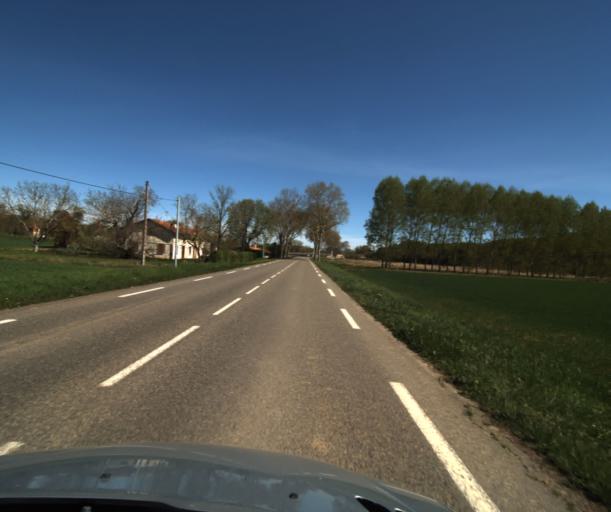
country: FR
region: Midi-Pyrenees
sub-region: Departement du Tarn-et-Garonne
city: Lafrancaise
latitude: 44.1330
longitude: 1.1876
